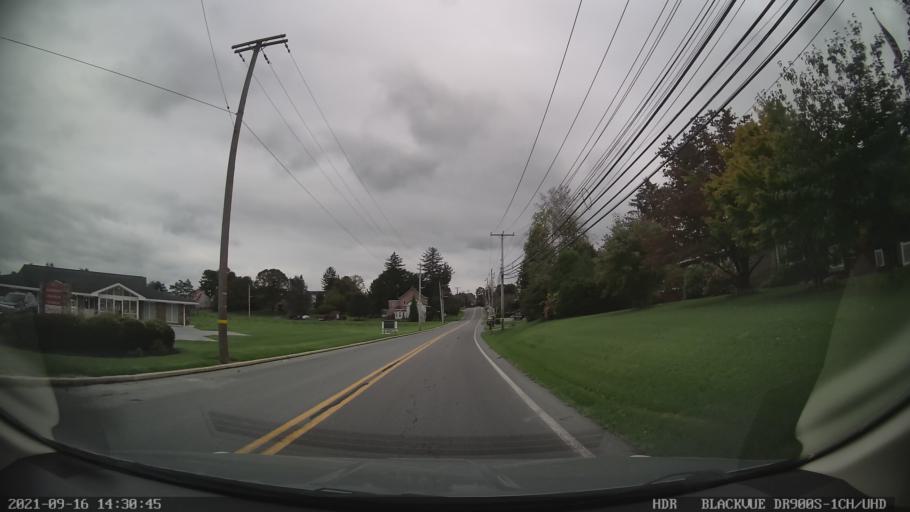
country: US
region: Pennsylvania
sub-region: Berks County
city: Kutztown
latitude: 40.5120
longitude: -75.7731
